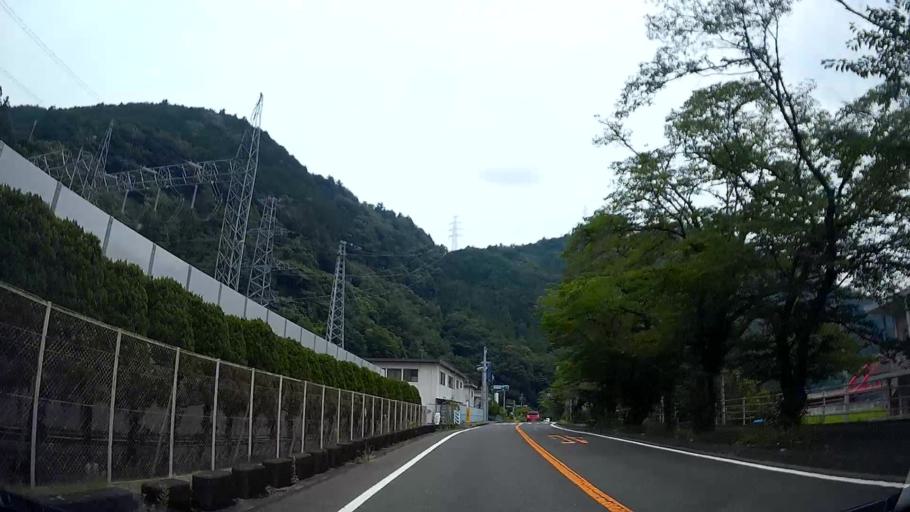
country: JP
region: Shizuoka
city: Mori
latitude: 35.0842
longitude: 137.7993
